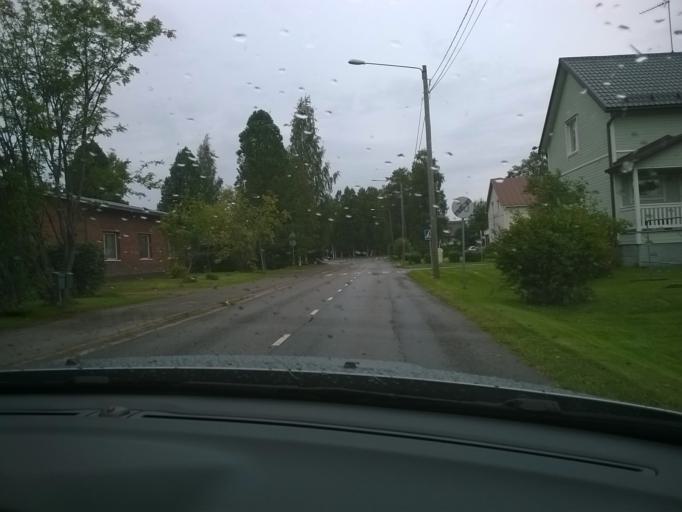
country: FI
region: Kainuu
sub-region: Kehys-Kainuu
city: Kuhmo
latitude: 64.1239
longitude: 29.5149
